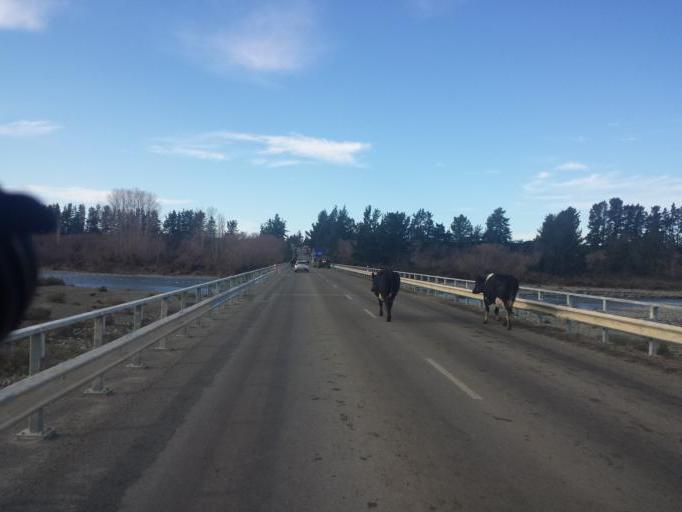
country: NZ
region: Canterbury
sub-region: Timaru District
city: Pleasant Point
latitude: -43.9741
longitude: 171.3014
